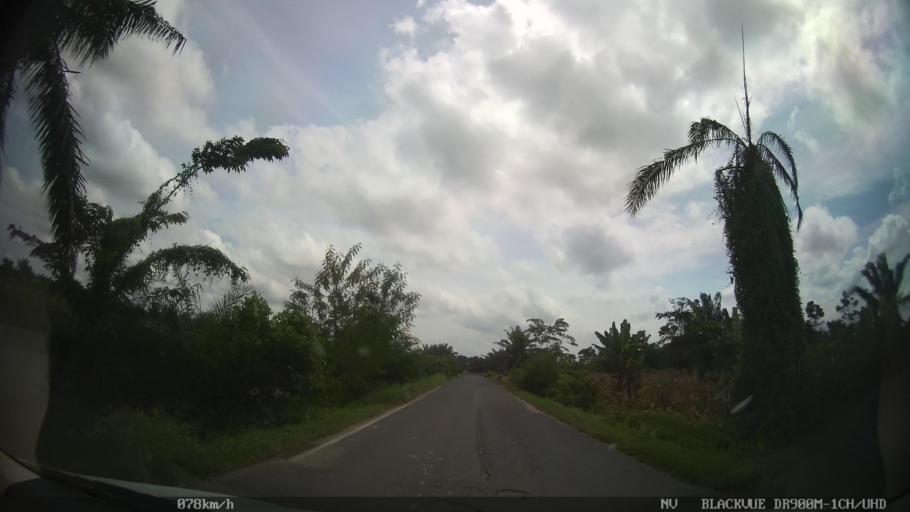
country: ID
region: North Sumatra
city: Percut
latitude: 3.6027
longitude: 98.8396
